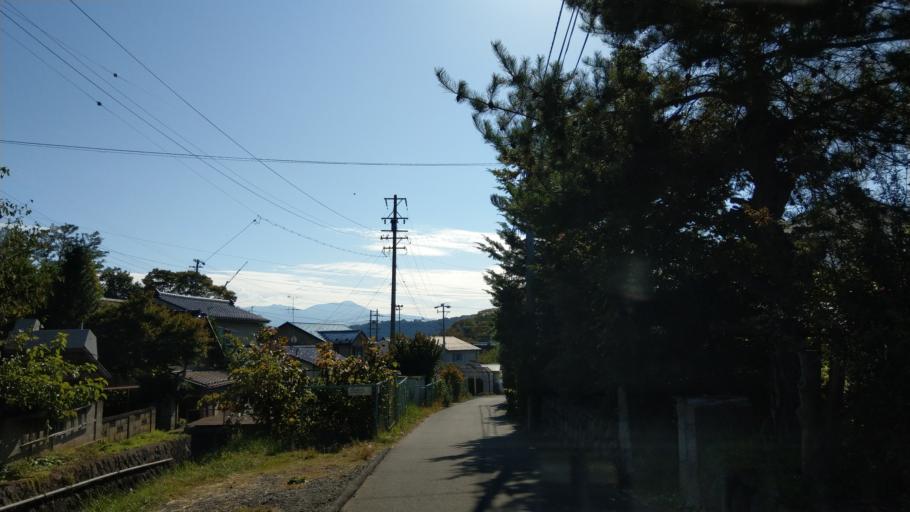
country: JP
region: Nagano
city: Komoro
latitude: 36.3332
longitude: 138.4309
